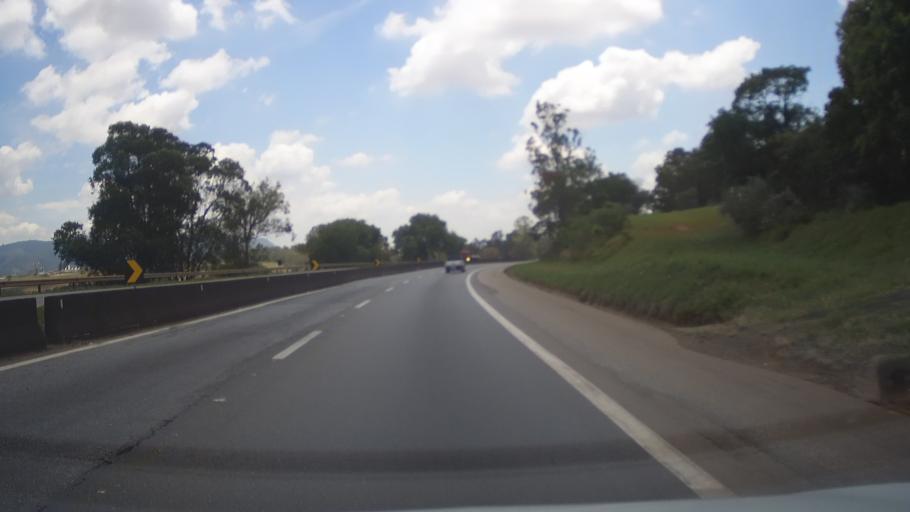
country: BR
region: Minas Gerais
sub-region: Sao Goncalo Do Sapucai
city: Sao Goncalo do Sapucai
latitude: -21.9428
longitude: -45.6185
